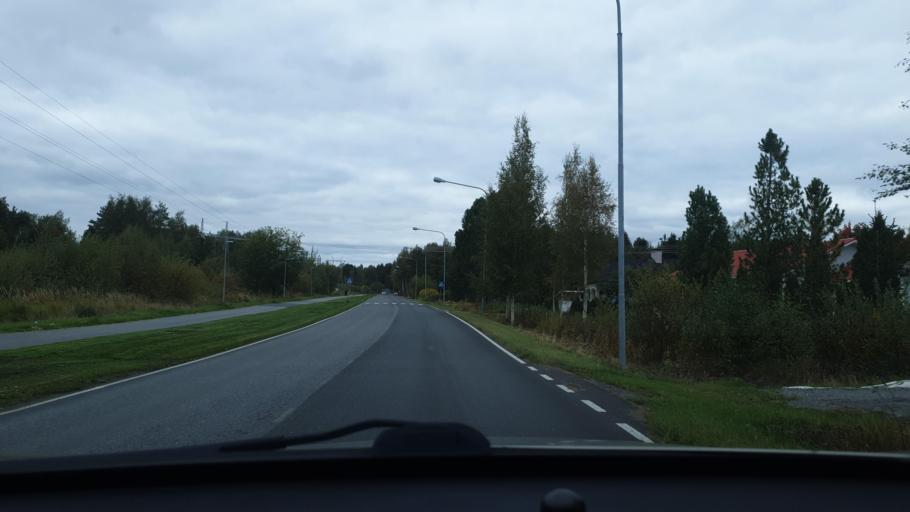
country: FI
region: Ostrobothnia
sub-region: Vaasa
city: Teeriniemi
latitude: 63.0906
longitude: 21.6995
